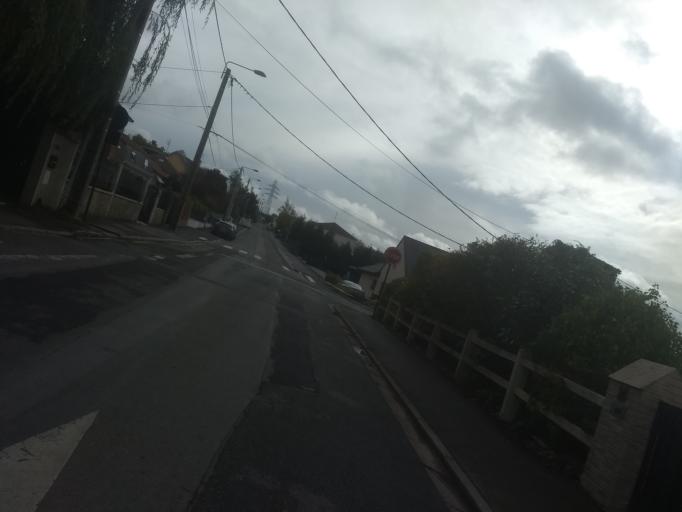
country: FR
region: Nord-Pas-de-Calais
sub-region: Departement du Pas-de-Calais
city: Anzin-Saint-Aubin
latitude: 50.3082
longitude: 2.7512
